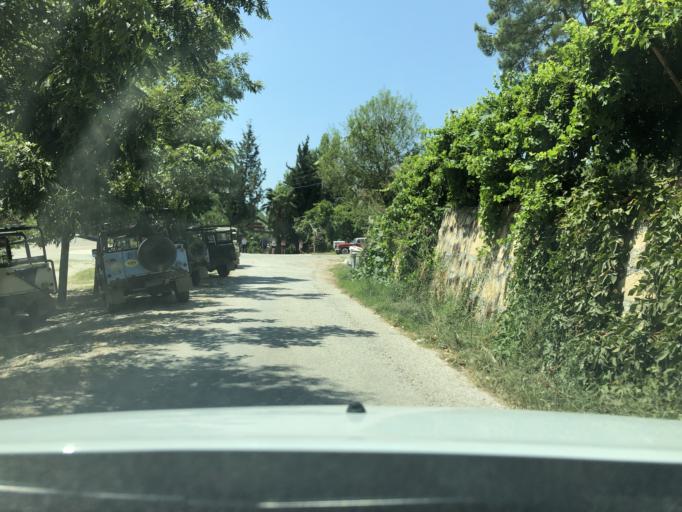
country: TR
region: Antalya
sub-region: Manavgat
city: Kizilagac
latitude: 36.8574
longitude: 31.5528
